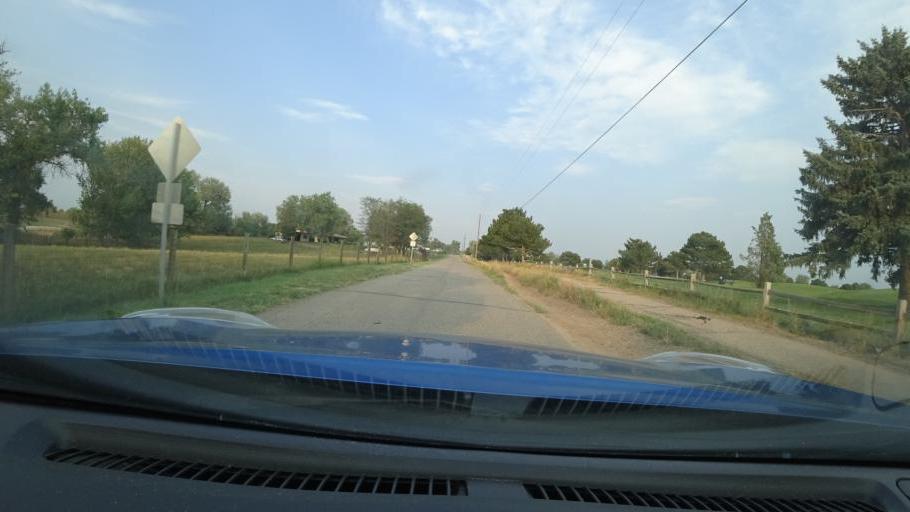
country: US
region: Colorado
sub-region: Adams County
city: Aurora
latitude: 39.7365
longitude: -104.7815
